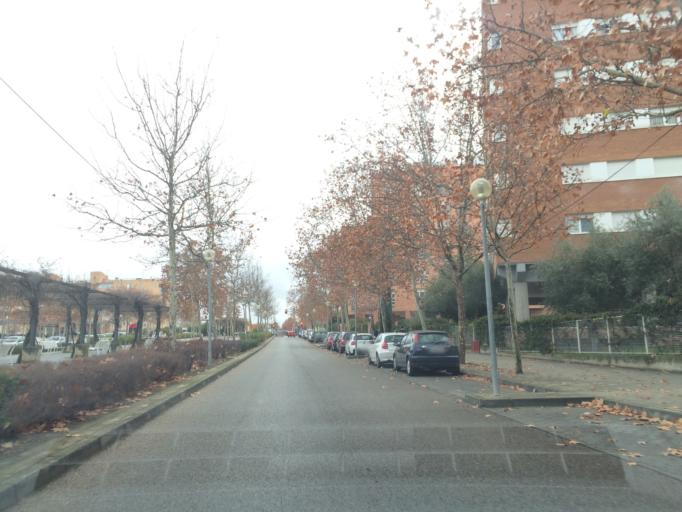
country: ES
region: Madrid
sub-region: Provincia de Madrid
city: Tres Cantos
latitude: 40.6016
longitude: -3.7136
